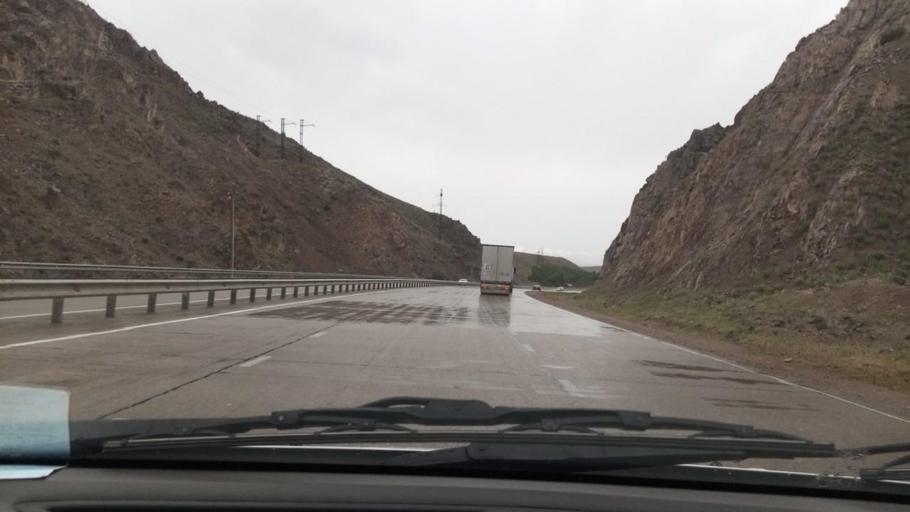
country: TJ
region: Viloyati Sughd
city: Shaydon
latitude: 40.9558
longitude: 70.6716
